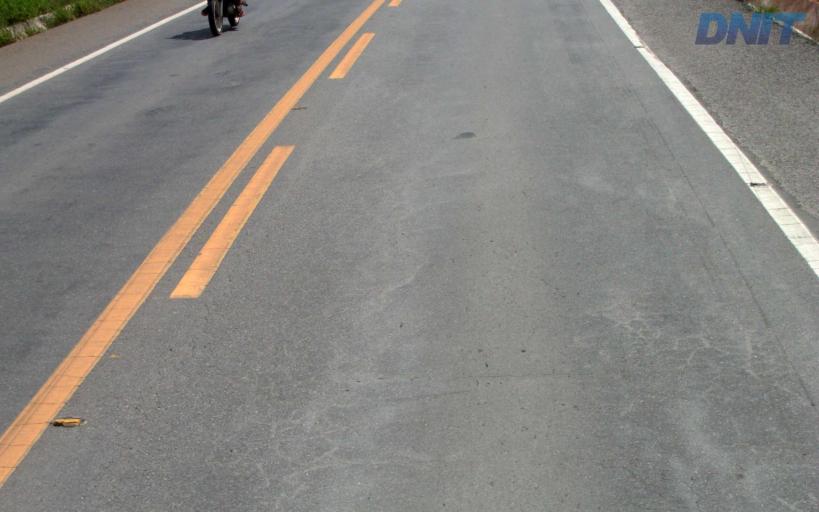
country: BR
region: Minas Gerais
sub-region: Governador Valadares
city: Governador Valadares
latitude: -19.0752
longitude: -42.1791
